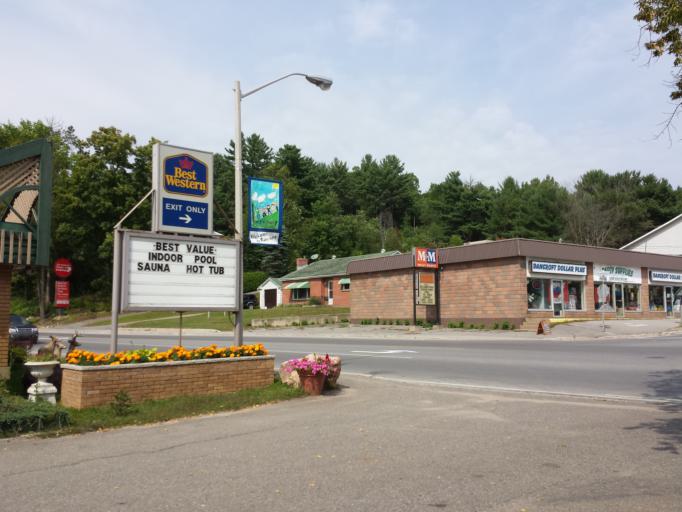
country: CA
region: Ontario
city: Bancroft
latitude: 45.0633
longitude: -77.8574
